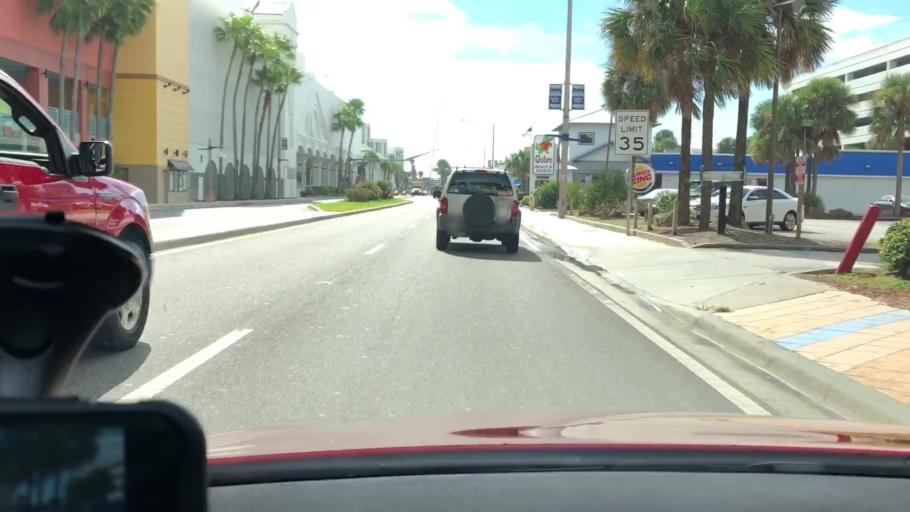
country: US
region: Florida
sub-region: Volusia County
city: Daytona Beach
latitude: 29.2311
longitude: -81.0104
